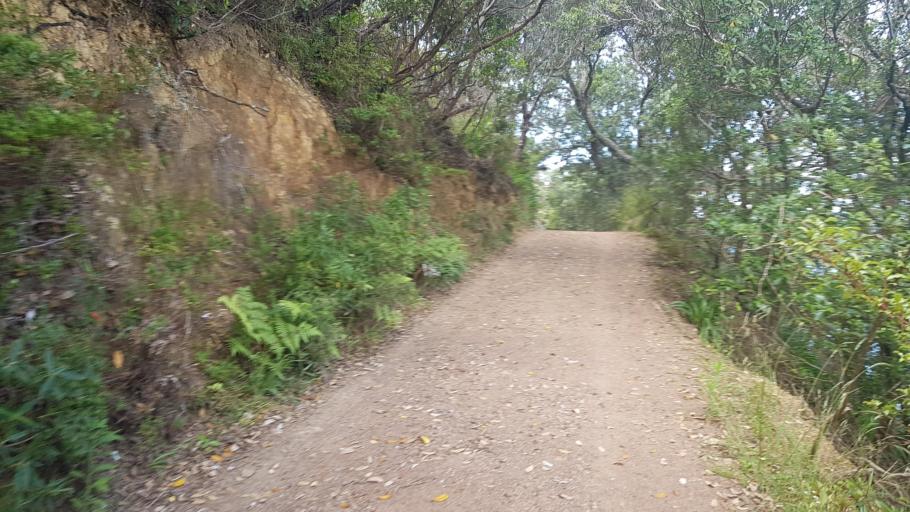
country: NZ
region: Auckland
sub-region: Auckland
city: Pakuranga
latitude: -36.8444
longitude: 175.1473
